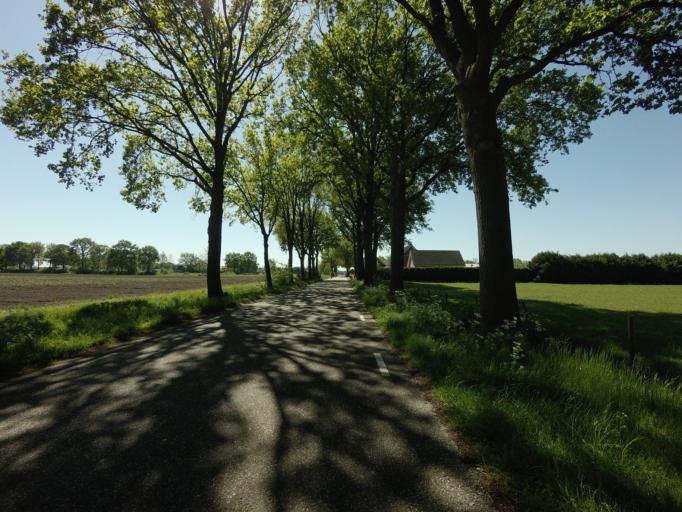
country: BE
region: Flanders
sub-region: Provincie Antwerpen
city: Essen
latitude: 51.4837
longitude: 4.4848
